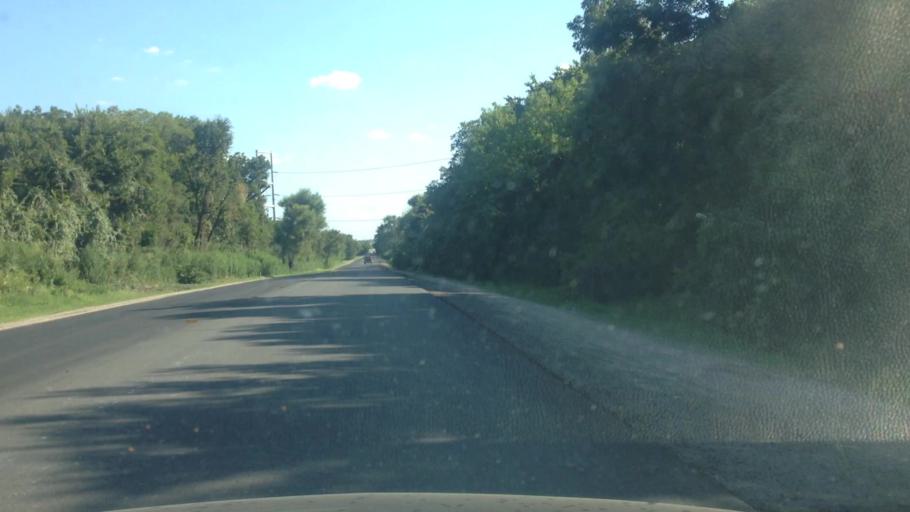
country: US
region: Texas
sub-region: Dallas County
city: Irving
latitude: 32.8654
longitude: -96.9163
